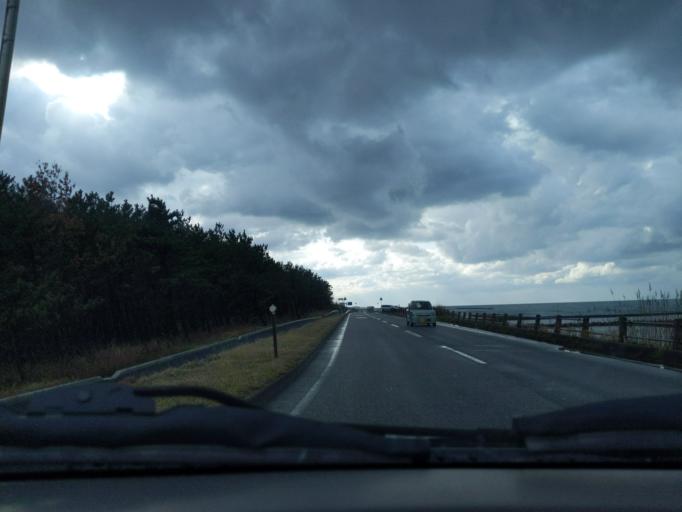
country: JP
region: Niigata
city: Niigata-shi
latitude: 37.9282
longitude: 139.0337
